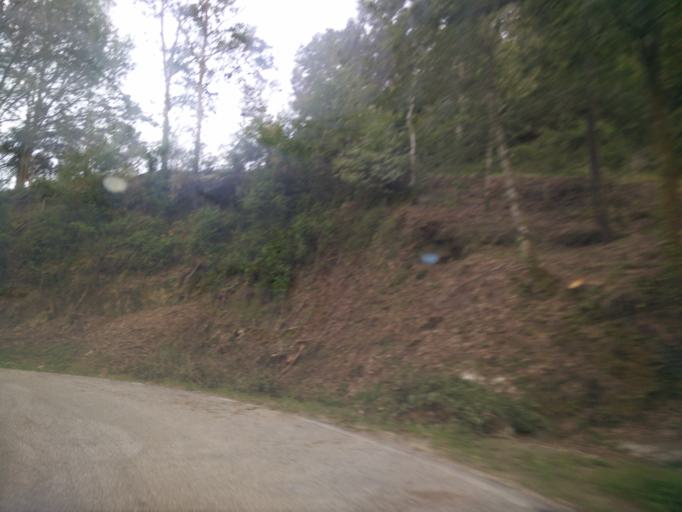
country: ES
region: Galicia
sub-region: Provincia de Pontevedra
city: Mondariz
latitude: 42.2690
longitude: -8.4082
